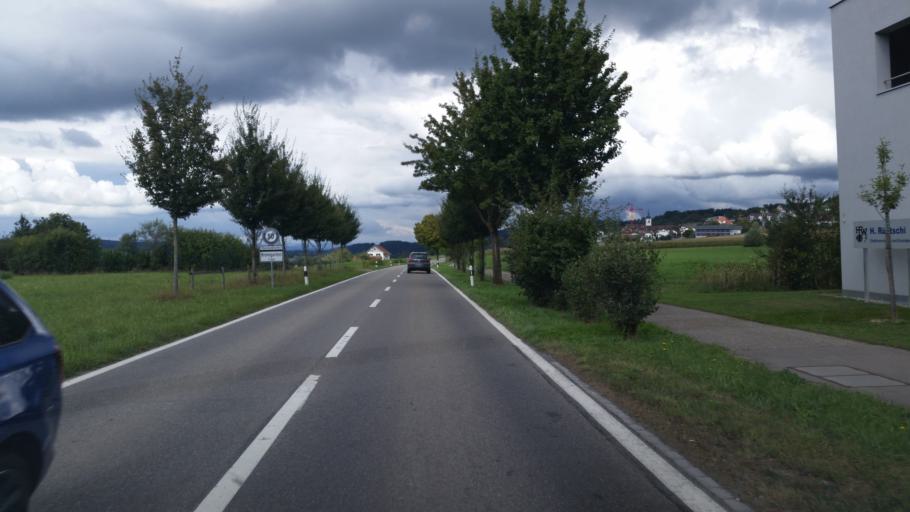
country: CH
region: Aargau
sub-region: Bezirk Bremgarten
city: Jonen
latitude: 47.3030
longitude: 8.3923
